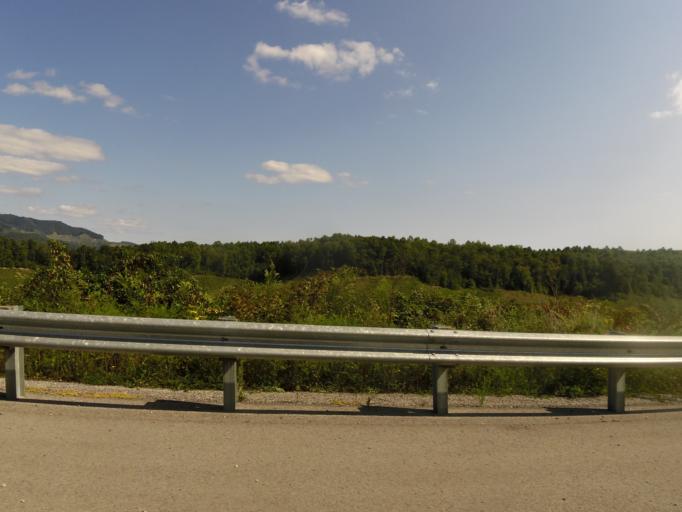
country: US
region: Kentucky
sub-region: Bell County
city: Pineville
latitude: 36.7422
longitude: -83.5910
